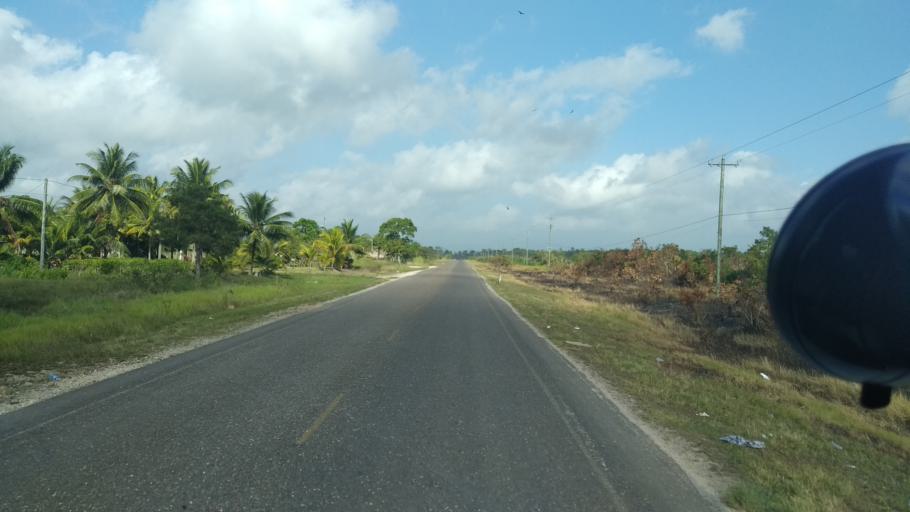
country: BZ
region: Stann Creek
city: Placencia
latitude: 16.5134
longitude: -88.5441
